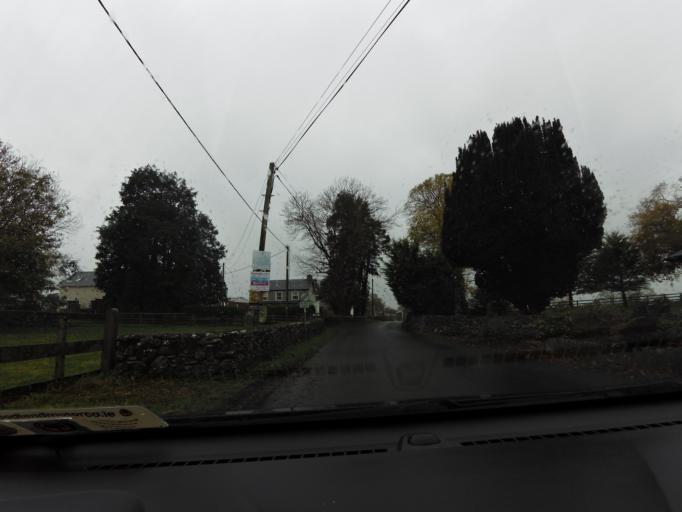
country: IE
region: Connaught
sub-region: County Galway
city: Gort
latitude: 53.0873
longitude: -8.8209
